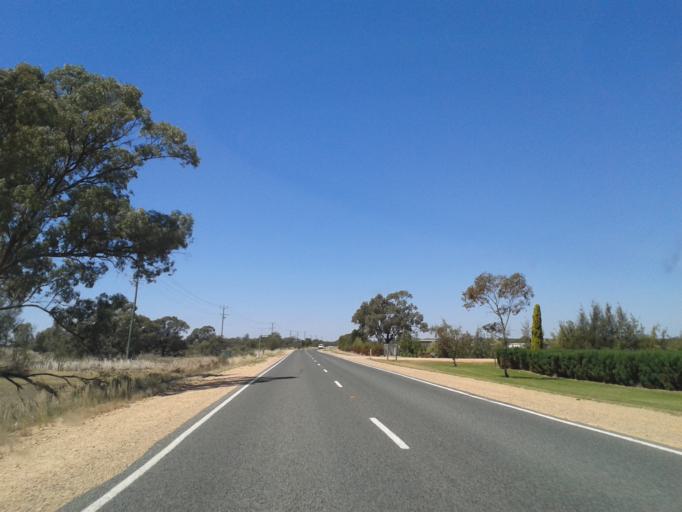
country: AU
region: Victoria
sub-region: Mildura Shire
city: Ouyen
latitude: -34.7098
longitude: 142.9031
